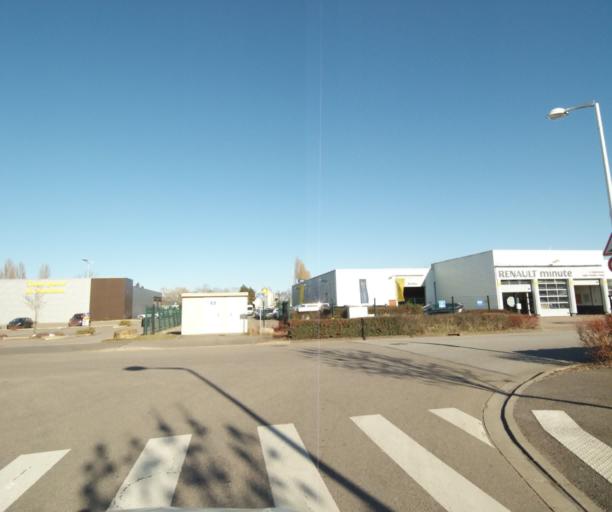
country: FR
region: Lorraine
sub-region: Departement de Meurthe-et-Moselle
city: Pulnoy
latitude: 48.7105
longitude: 6.2469
